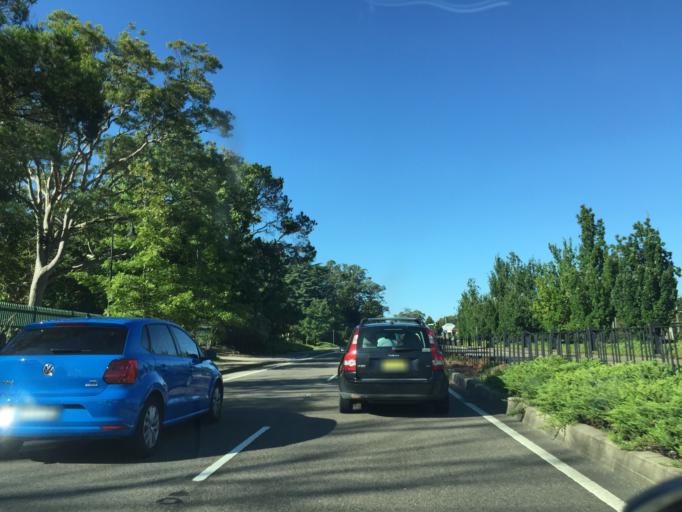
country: AU
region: New South Wales
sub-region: Blue Mountains Municipality
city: Hazelbrook
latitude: -33.6960
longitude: 150.5350
